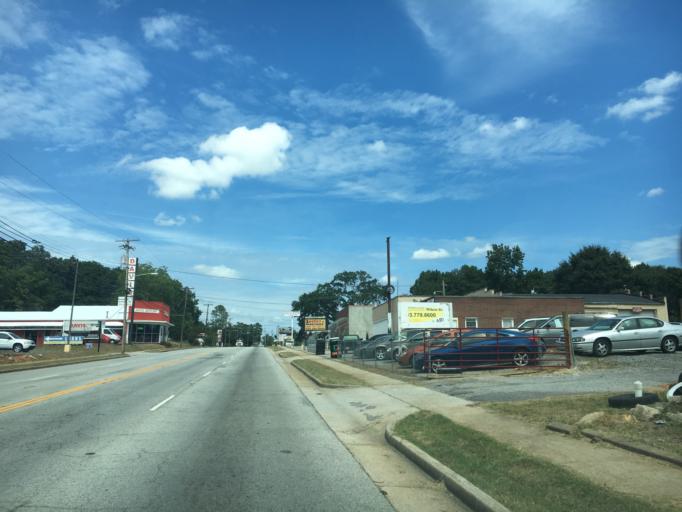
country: US
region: South Carolina
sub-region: Laurens County
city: Laurens
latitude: 34.5081
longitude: -82.0075
